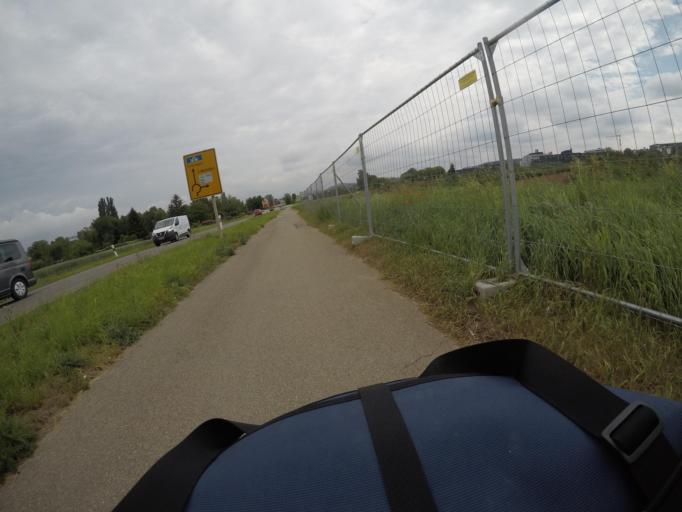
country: DE
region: Baden-Wuerttemberg
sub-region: Regierungsbezirk Stuttgart
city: Gerlingen
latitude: 48.8060
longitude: 9.0667
